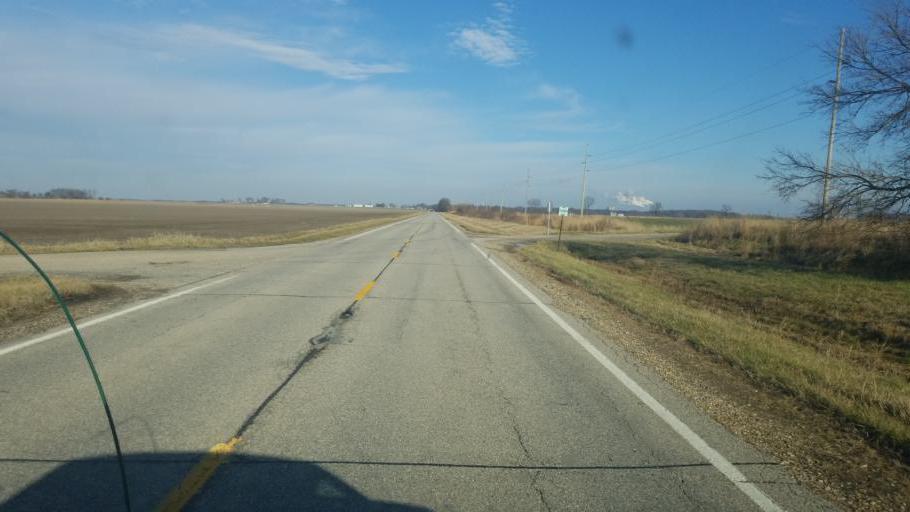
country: US
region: Illinois
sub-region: Edwards County
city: Grayville
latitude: 38.3337
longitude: -87.8991
